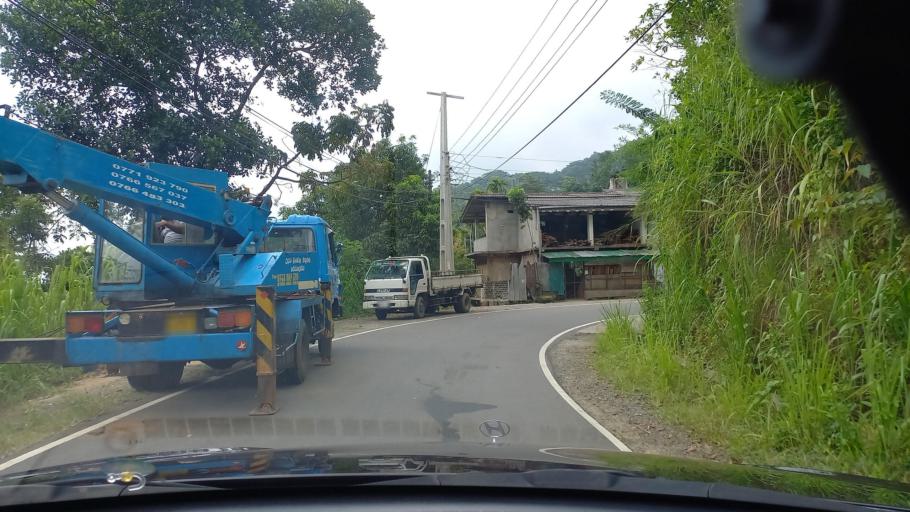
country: LK
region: Central
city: Gampola
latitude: 7.2278
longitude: 80.6051
